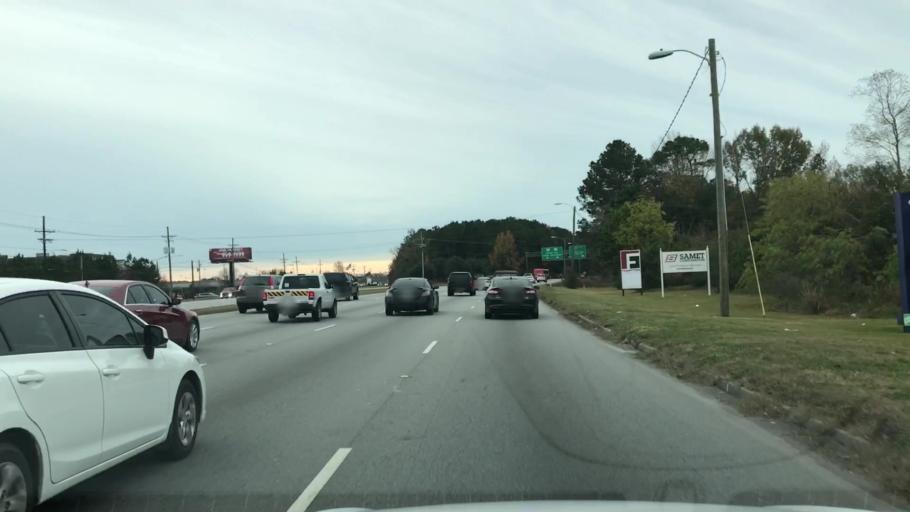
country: US
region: South Carolina
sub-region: Berkeley County
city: Goose Creek
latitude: 32.9535
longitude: -80.0425
